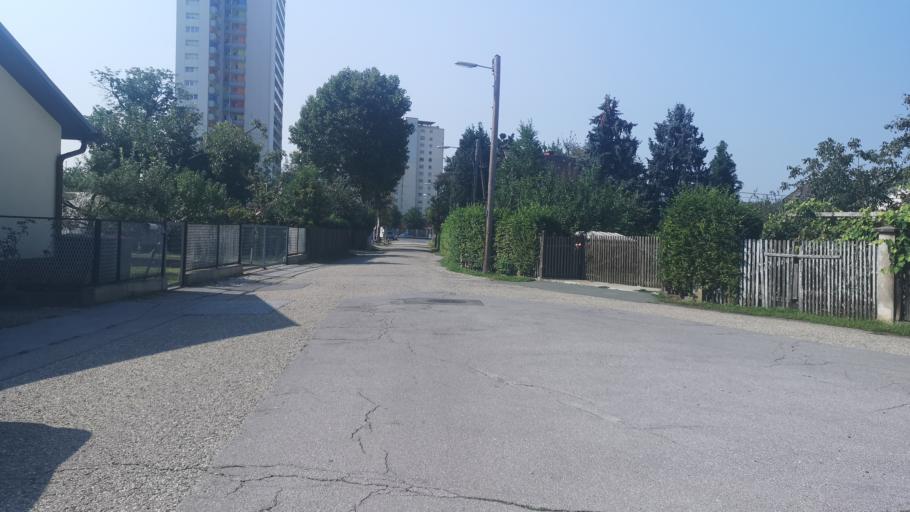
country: AT
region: Styria
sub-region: Graz Stadt
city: Wetzelsdorf
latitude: 47.0419
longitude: 15.4124
